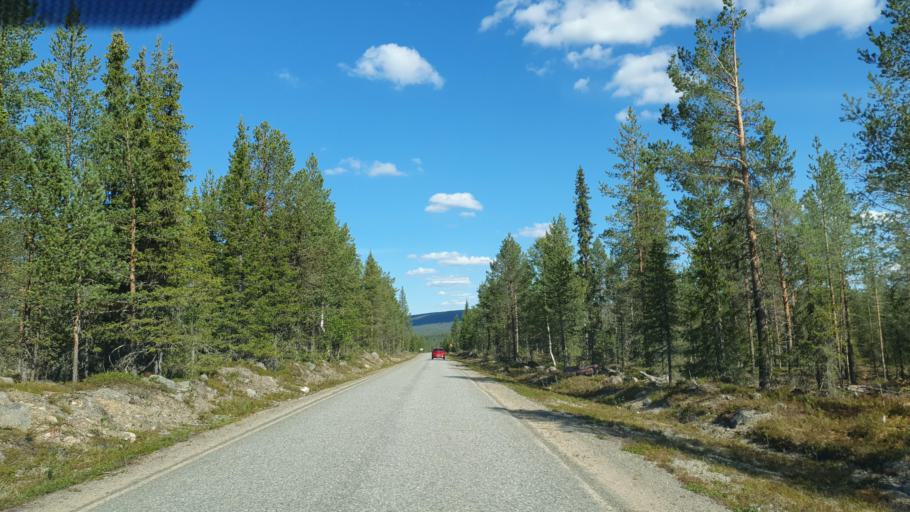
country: FI
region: Lapland
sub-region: Tunturi-Lappi
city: Muonio
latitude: 67.6981
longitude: 24.1155
